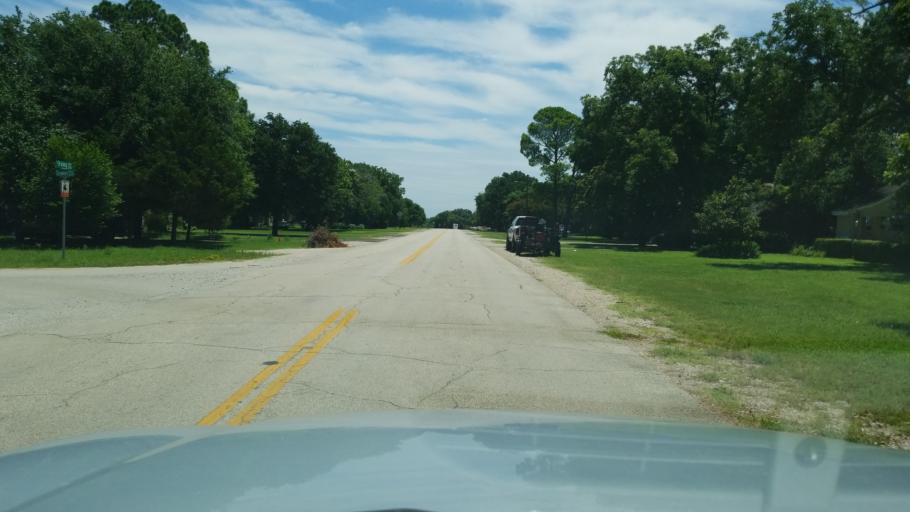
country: US
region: Texas
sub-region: Dallas County
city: Irving
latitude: 32.8023
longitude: -96.9118
